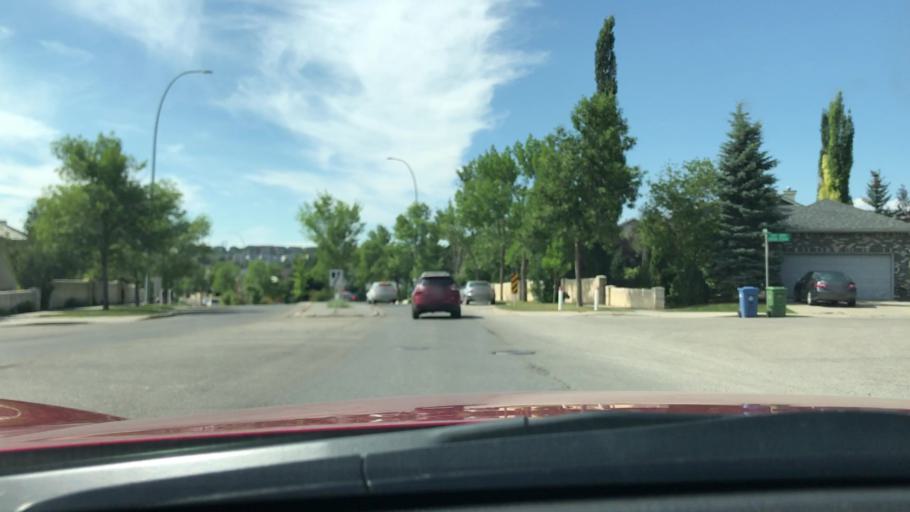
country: CA
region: Alberta
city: Calgary
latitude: 51.0201
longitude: -114.1791
